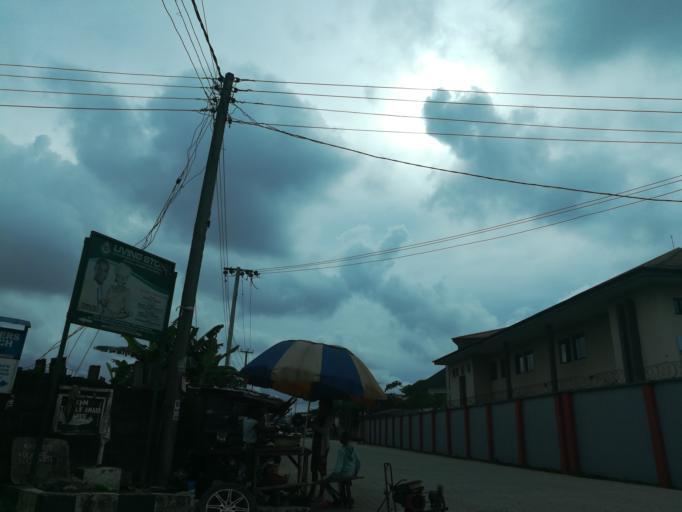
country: NG
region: Rivers
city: Port Harcourt
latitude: 4.8117
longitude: 6.9903
